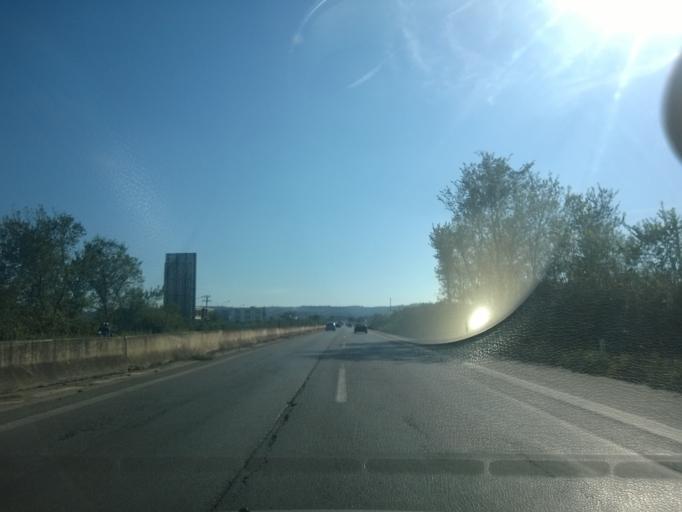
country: GR
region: Central Macedonia
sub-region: Nomos Thessalonikis
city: Neo Rysi
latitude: 40.5140
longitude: 23.0091
